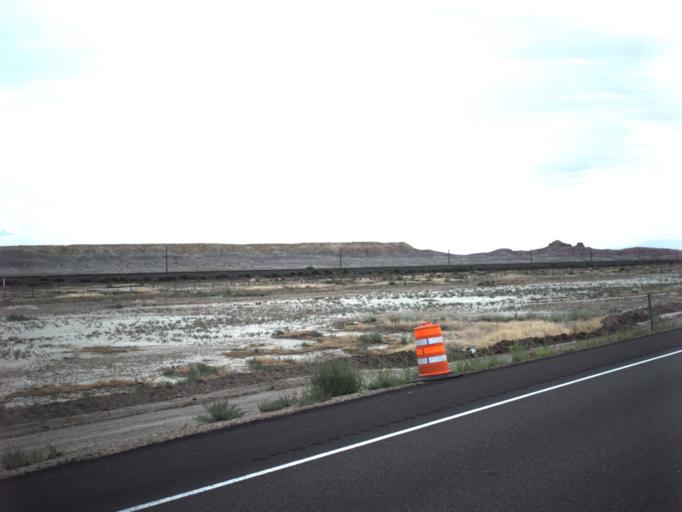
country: US
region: Utah
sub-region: Carbon County
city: East Carbon City
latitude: 39.0208
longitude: -110.2941
